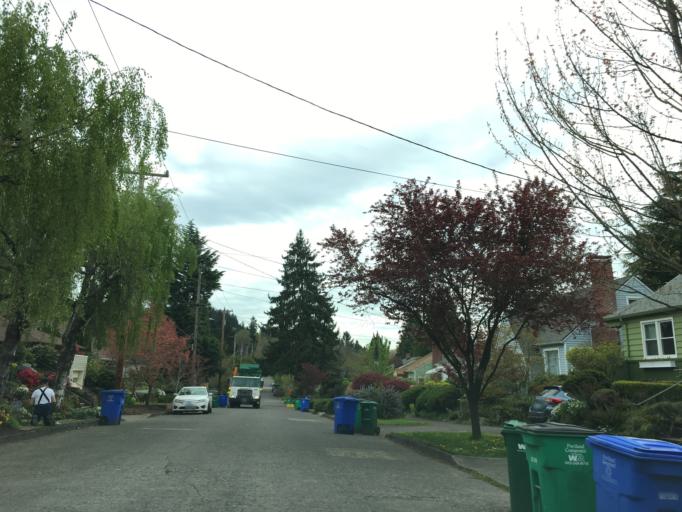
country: US
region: Oregon
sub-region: Multnomah County
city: Lents
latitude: 45.5254
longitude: -122.5996
